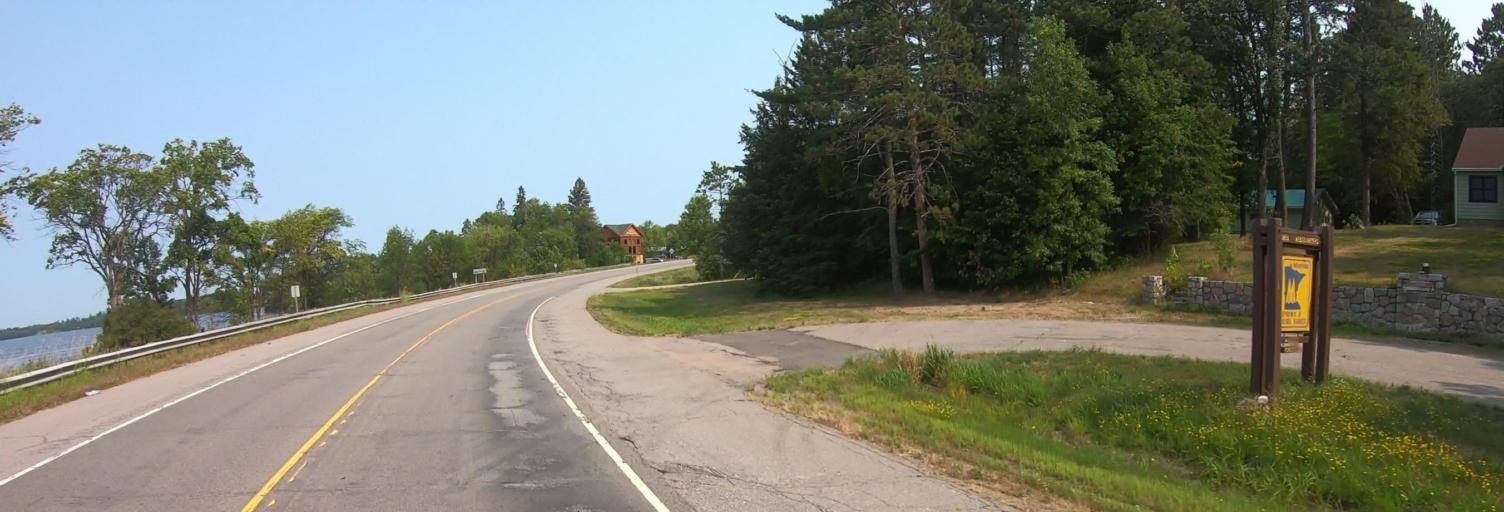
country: US
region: Minnesota
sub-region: Saint Louis County
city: Mountain Iron
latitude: 48.0608
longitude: -92.8309
